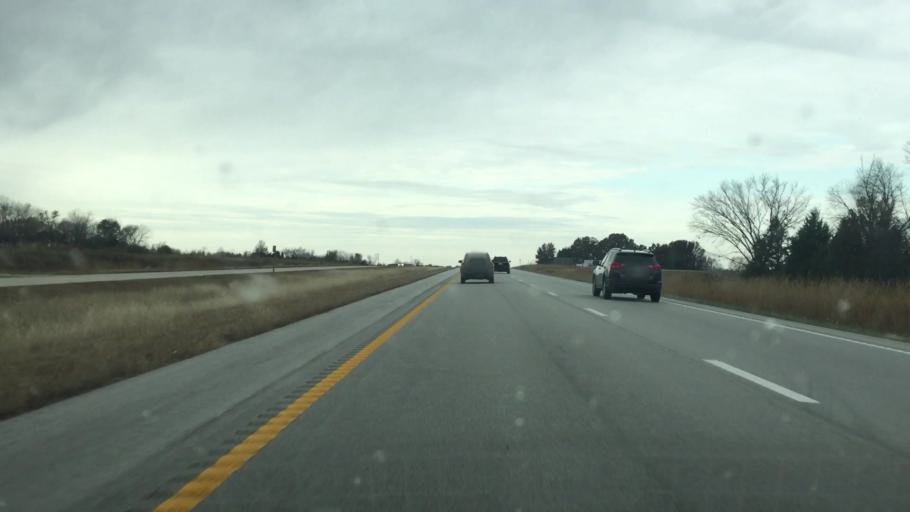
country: US
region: Missouri
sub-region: Saint Clair County
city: Osceola
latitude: 38.1799
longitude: -93.7267
